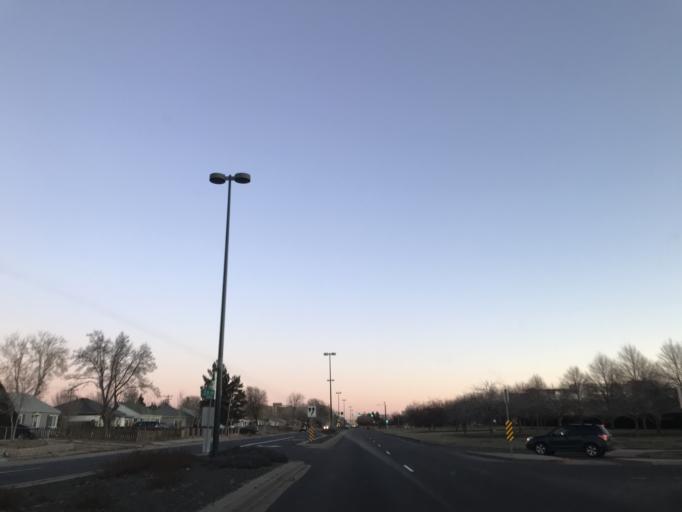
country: US
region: Colorado
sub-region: Arapahoe County
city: Glendale
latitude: 39.7557
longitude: -104.9033
